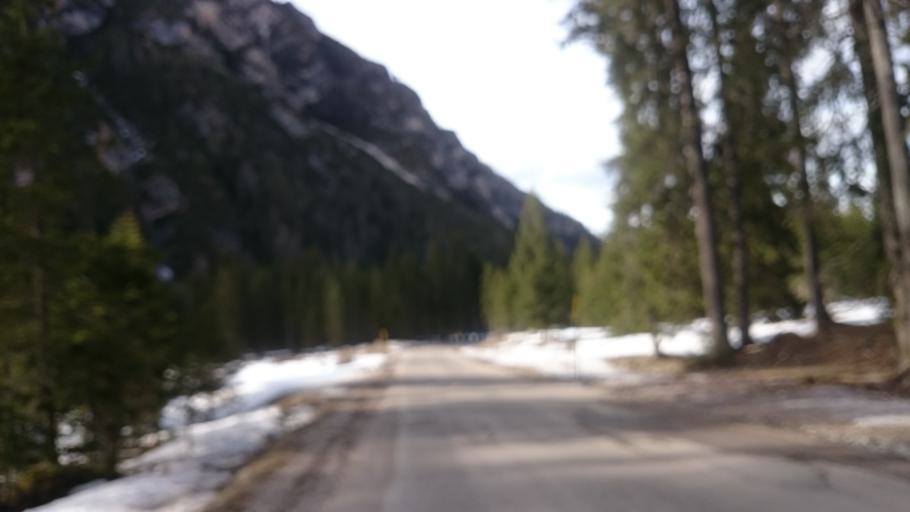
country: IT
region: Trentino-Alto Adige
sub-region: Bolzano
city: Braies
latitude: 46.6727
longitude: 12.1492
